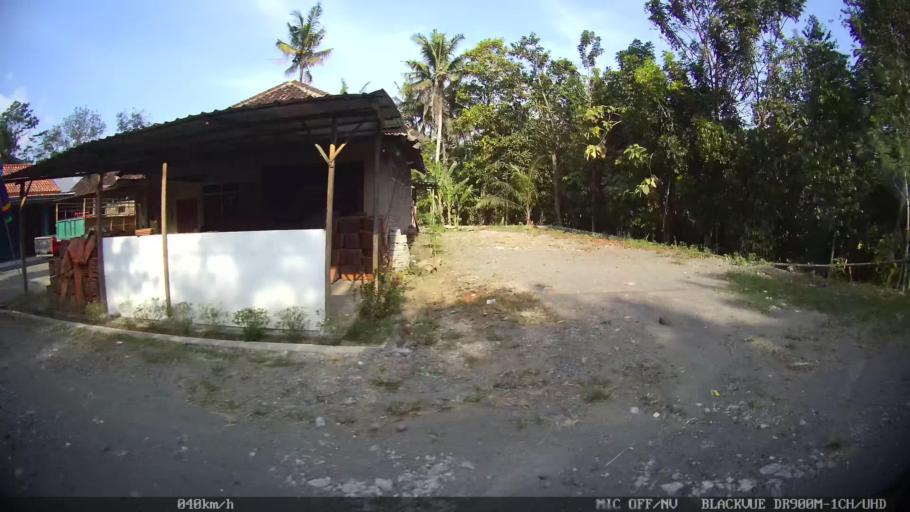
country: ID
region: Daerah Istimewa Yogyakarta
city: Bantul
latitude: -7.8769
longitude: 110.3148
